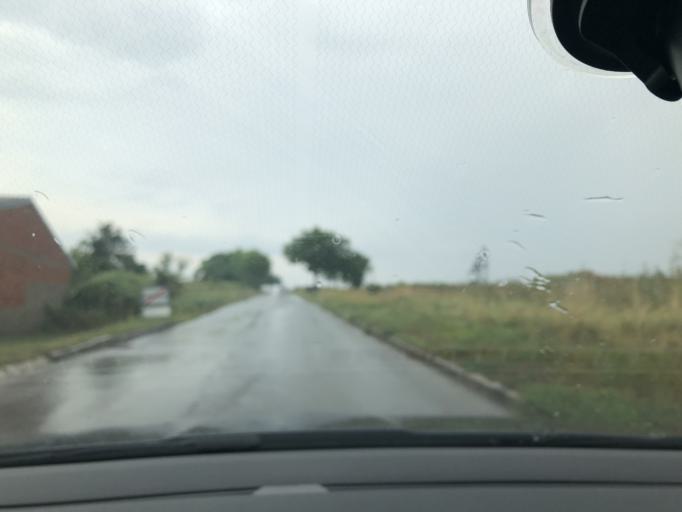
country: AT
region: Lower Austria
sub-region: Politischer Bezirk Ganserndorf
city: Auersthal
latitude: 48.3742
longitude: 16.6423
